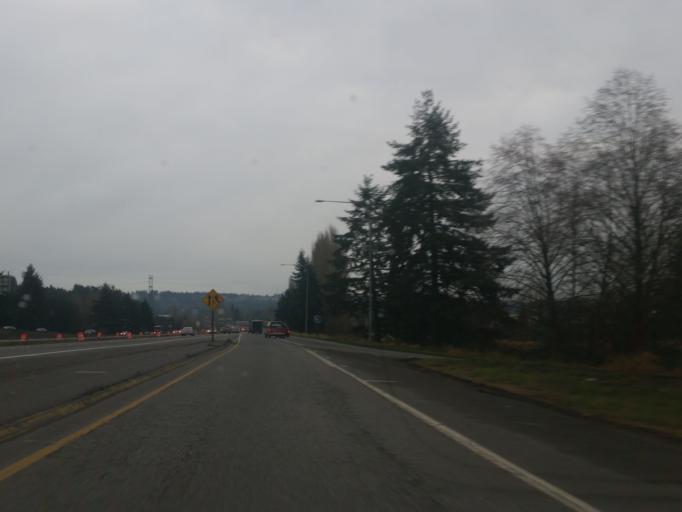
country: US
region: Washington
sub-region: King County
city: Woodinville
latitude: 47.7586
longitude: -122.1812
